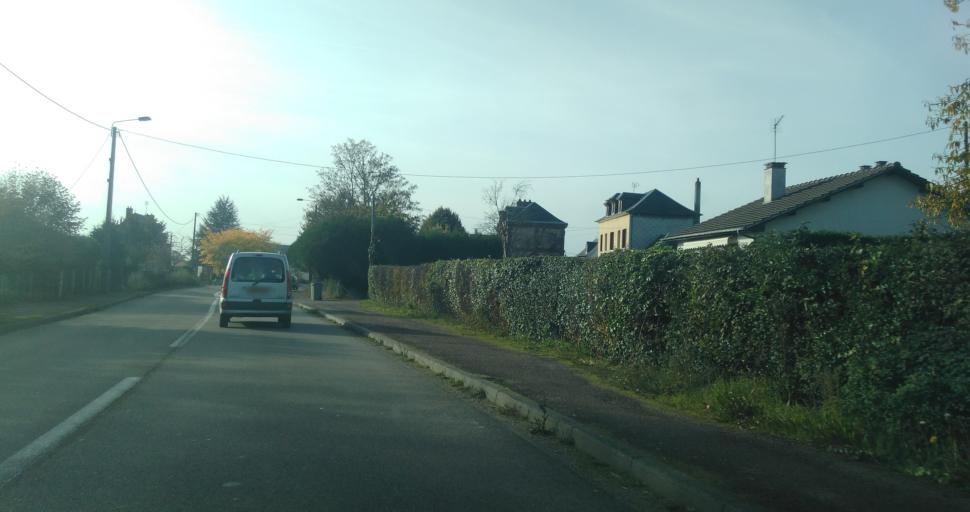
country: FR
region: Haute-Normandie
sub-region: Departement de l'Eure
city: Saint-Ouen-de-Thouberville
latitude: 49.3565
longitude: 0.8869
